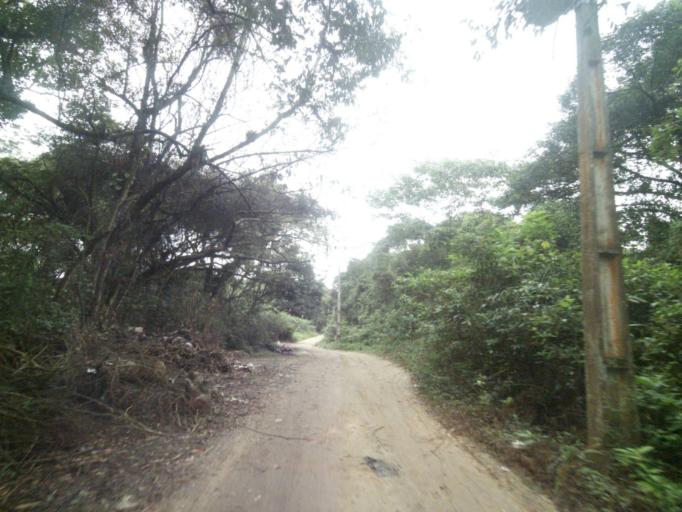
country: BR
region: Parana
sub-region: Paranagua
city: Paranagua
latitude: -25.5393
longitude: -48.5524
